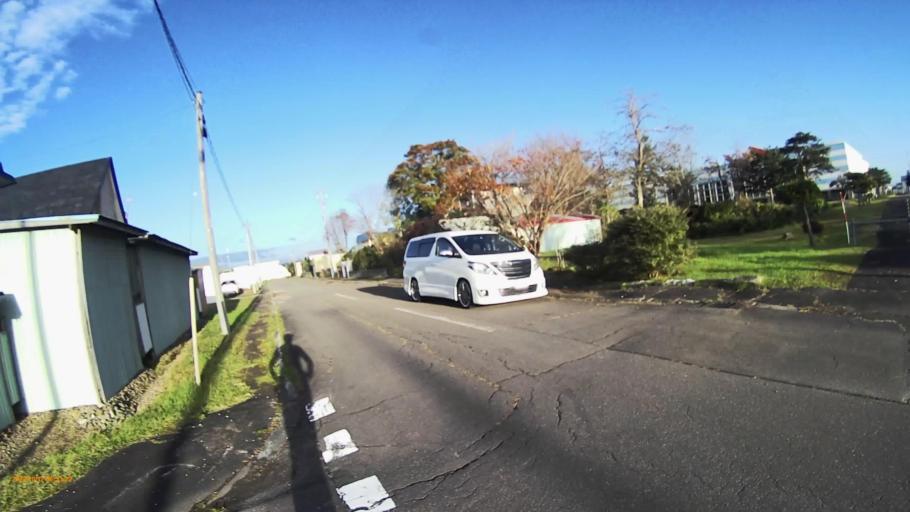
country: JP
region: Hokkaido
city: Kushiro
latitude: 42.8914
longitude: 143.9349
